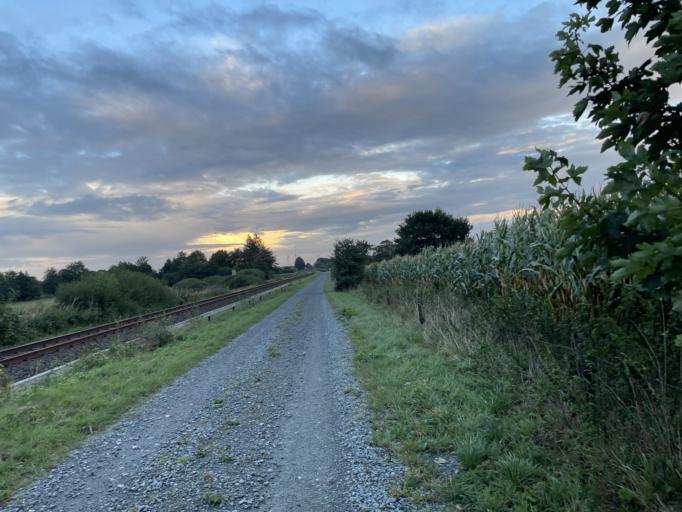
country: DE
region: Schleswig-Holstein
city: Mildstedt
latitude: 54.4776
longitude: 9.1160
